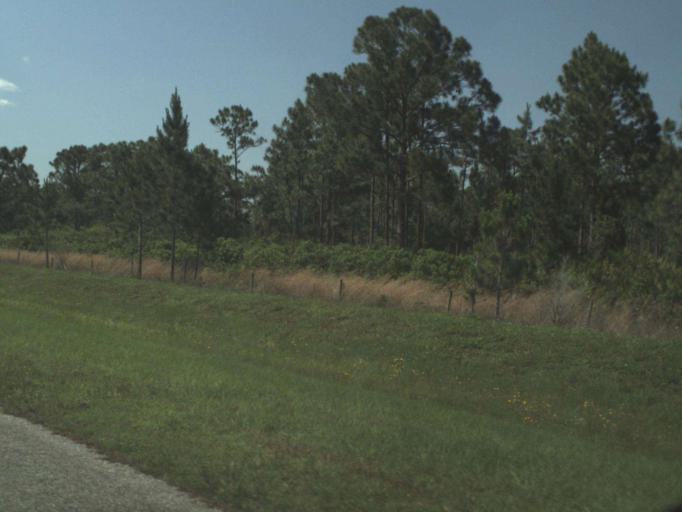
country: US
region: Florida
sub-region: Orange County
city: Wedgefield
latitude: 28.4851
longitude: -81.0332
